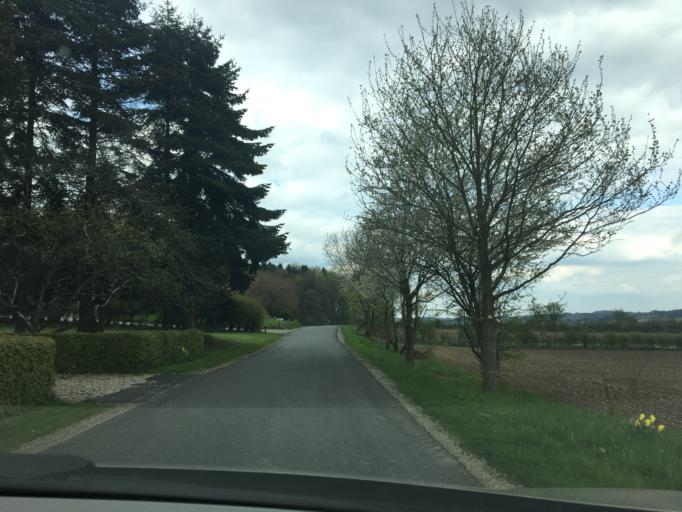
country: DK
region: Central Jutland
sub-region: Horsens Kommune
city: Braedstrup
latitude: 55.9749
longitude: 9.6846
